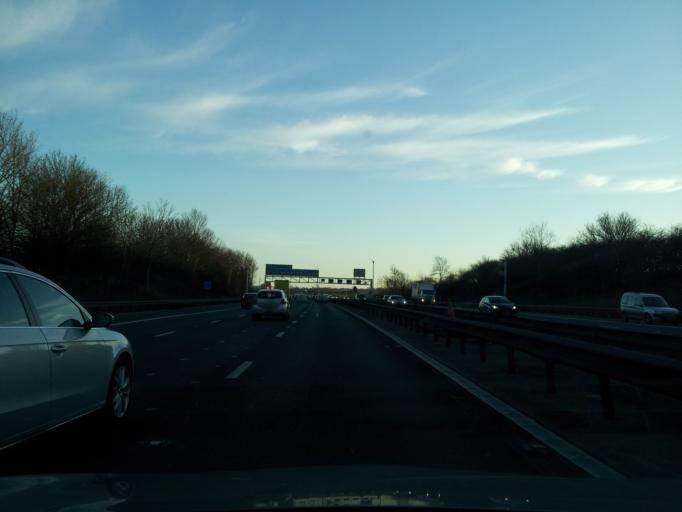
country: GB
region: England
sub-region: Central Bedfordshire
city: Toddington
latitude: 51.9744
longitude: -0.5262
